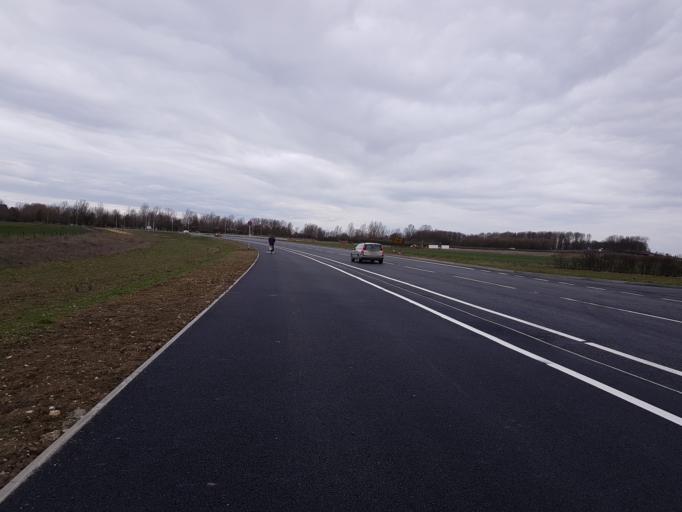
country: GB
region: England
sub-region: Cambridgeshire
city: Girton
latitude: 52.2429
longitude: 0.0429
